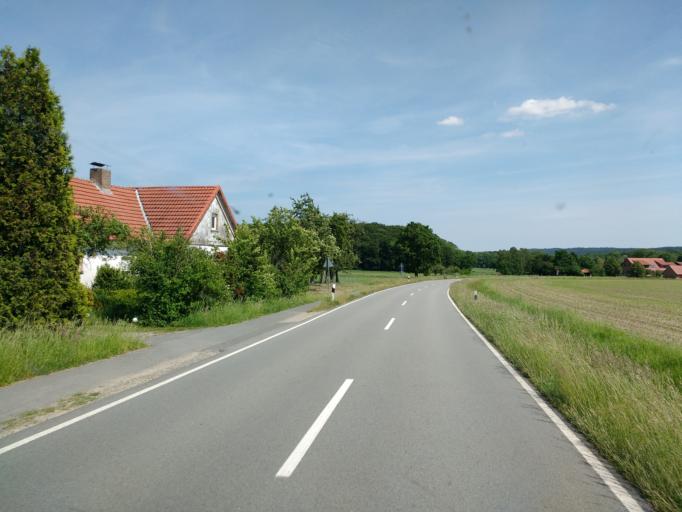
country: DE
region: Lower Saxony
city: Belm
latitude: 52.3757
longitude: 8.1003
